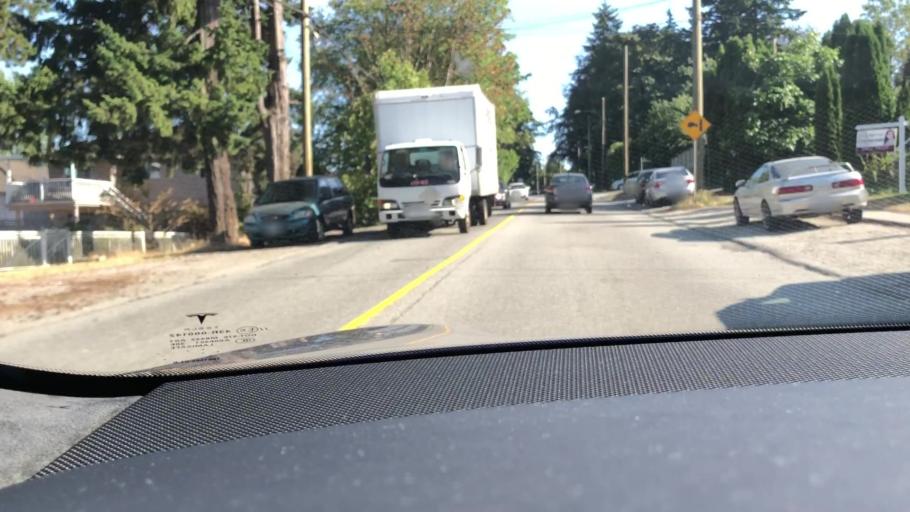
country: CA
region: British Columbia
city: Burnaby
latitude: 49.2542
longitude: -122.9820
